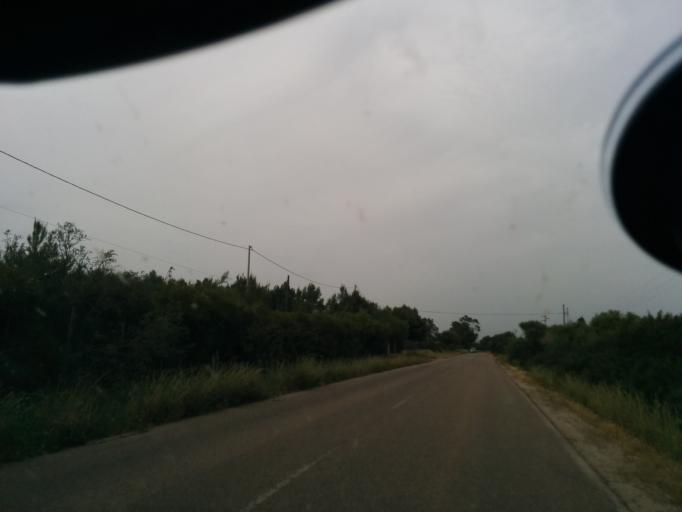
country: IT
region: Sardinia
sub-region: Provincia di Carbonia-Iglesias
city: Sant'Antioco
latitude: 39.0285
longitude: 8.4506
